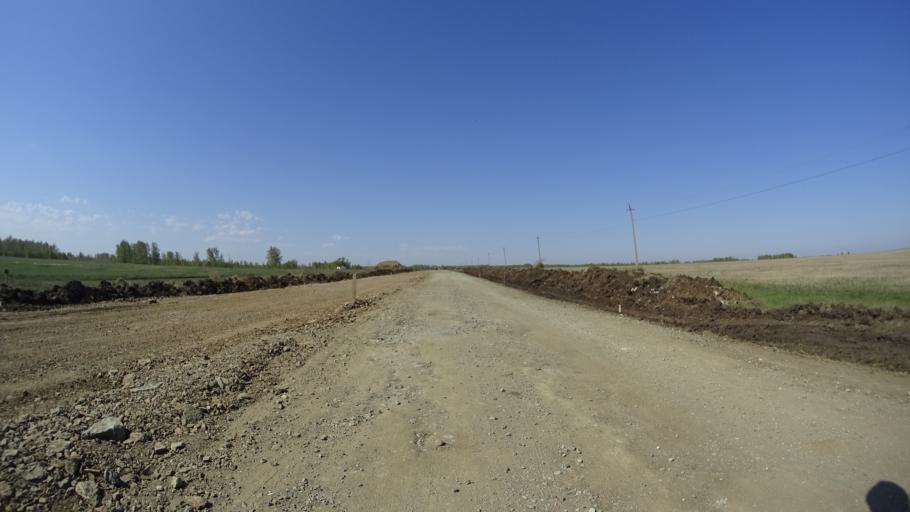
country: RU
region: Chelyabinsk
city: Troitsk
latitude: 54.1836
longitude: 61.4893
